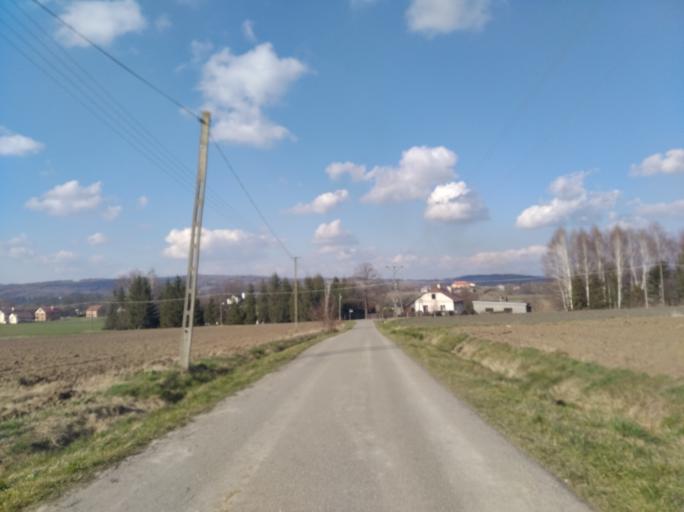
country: PL
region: Subcarpathian Voivodeship
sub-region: Powiat strzyzowski
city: Wysoka Strzyzowska
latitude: 49.8546
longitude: 21.7094
